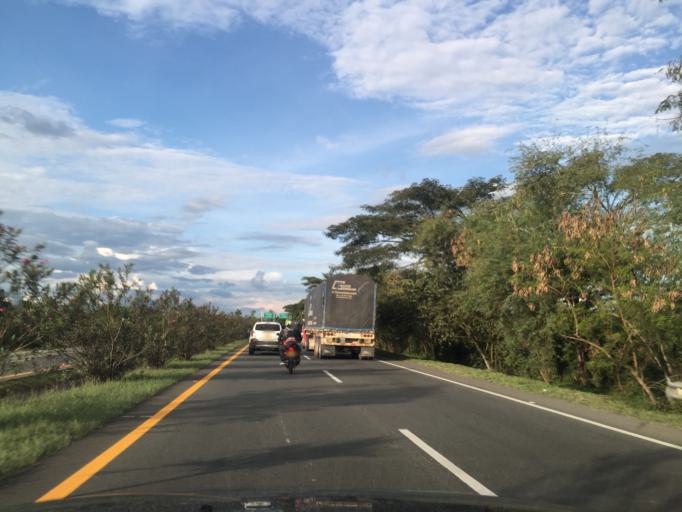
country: CO
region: Valle del Cauca
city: Andalucia
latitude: 4.1880
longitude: -76.1680
